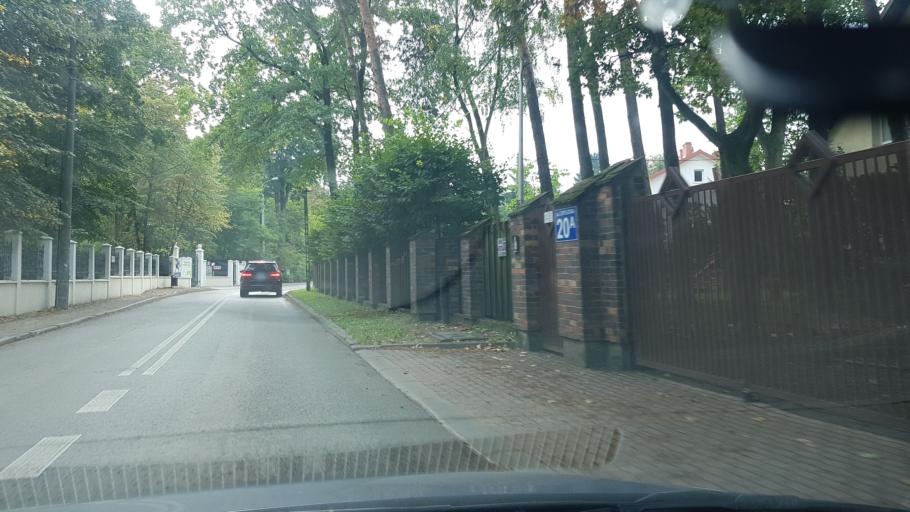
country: PL
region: Masovian Voivodeship
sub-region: Powiat piaseczynski
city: Konstancin-Jeziorna
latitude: 52.0793
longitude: 21.0977
